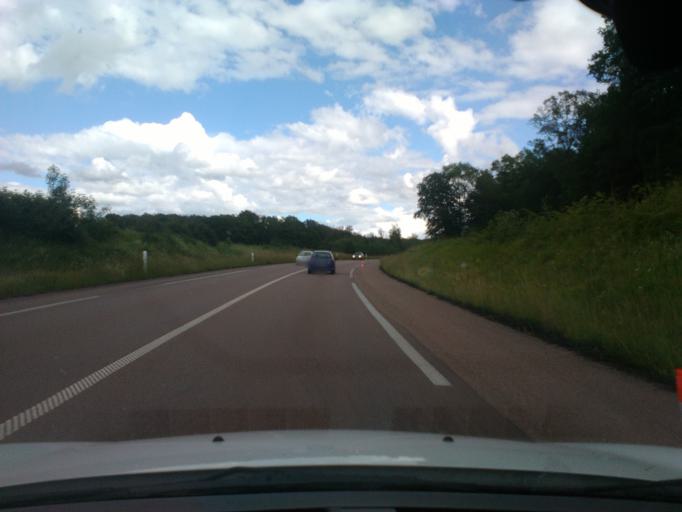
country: FR
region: Lorraine
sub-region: Departement des Vosges
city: Uxegney
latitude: 48.2054
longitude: 6.3868
